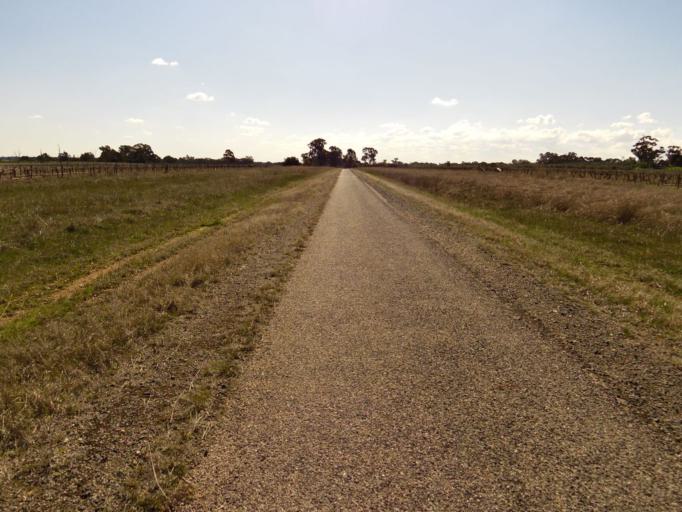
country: AU
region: New South Wales
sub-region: Corowa Shire
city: Corowa
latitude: -36.0438
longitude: 146.4562
